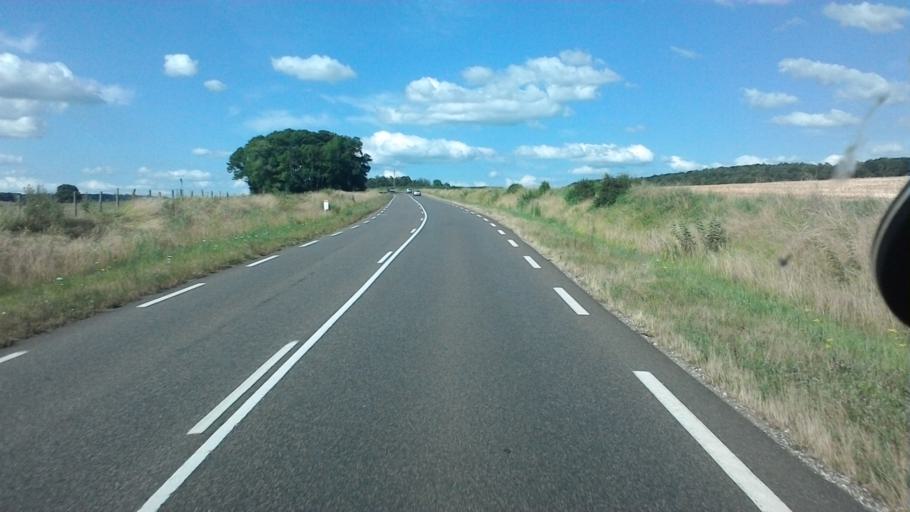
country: FR
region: Franche-Comte
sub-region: Departement de la Haute-Saone
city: Echenoz-la-Meline
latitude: 47.5500
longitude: 6.0616
